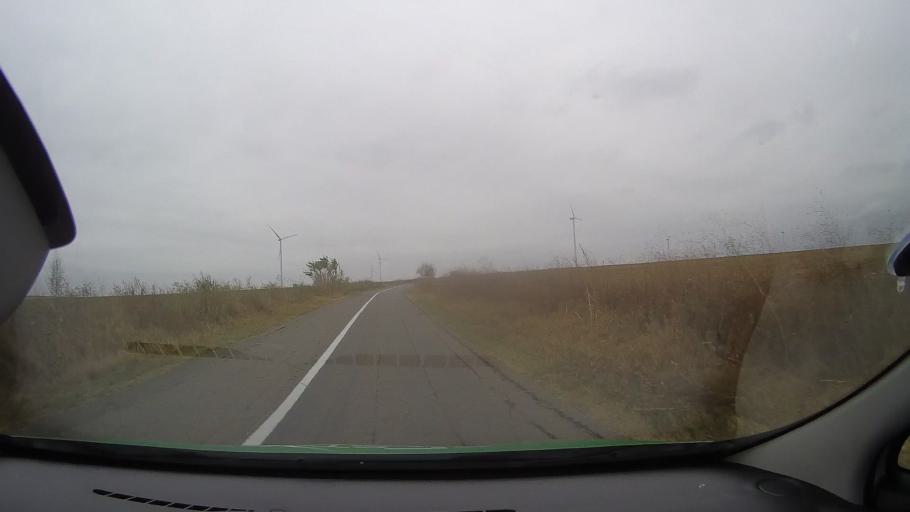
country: RO
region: Constanta
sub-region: Comuna Pantelimon
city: Pantelimon
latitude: 44.5019
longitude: 28.3527
